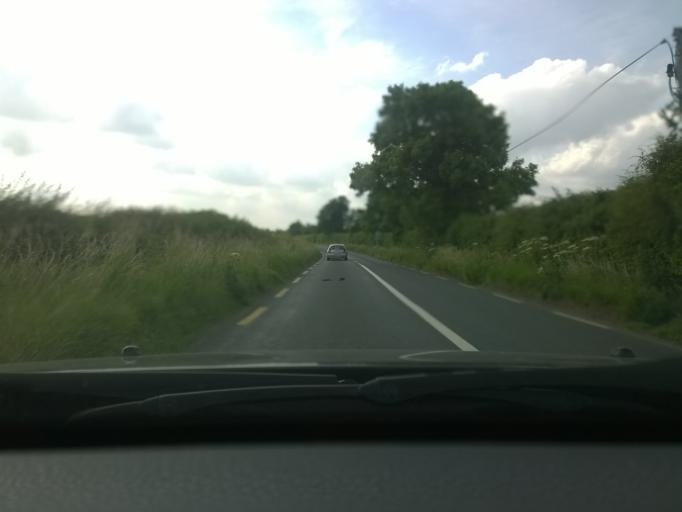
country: IE
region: Leinster
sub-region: Kildare
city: Rathangan
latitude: 53.2156
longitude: -6.9739
